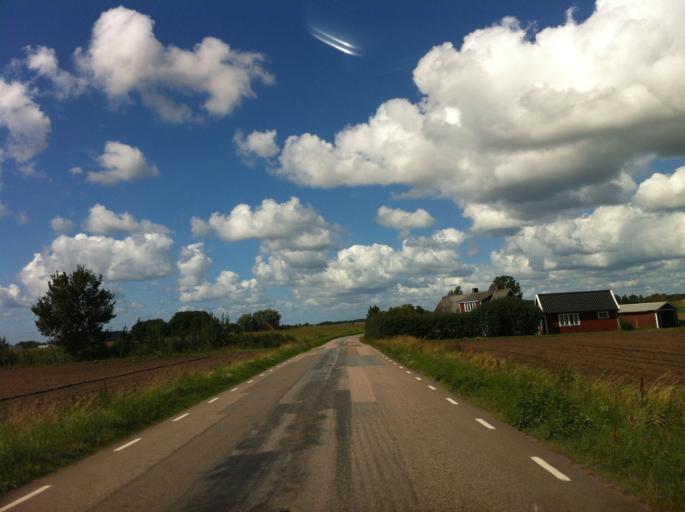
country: SE
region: Skane
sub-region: Angelholms Kommun
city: AEngelholm
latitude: 56.2521
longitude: 12.8762
